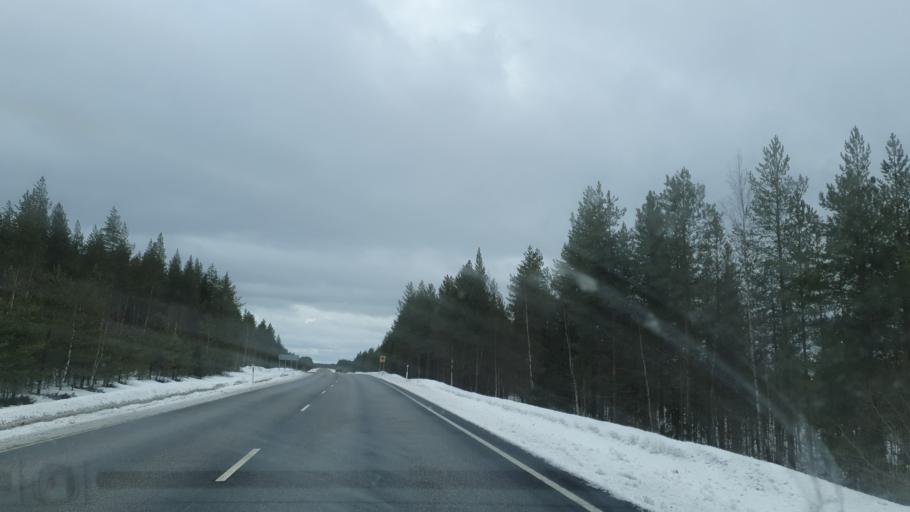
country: FI
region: Northern Ostrobothnia
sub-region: Oulunkaari
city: Pudasjaervi
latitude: 65.4148
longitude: 26.8821
